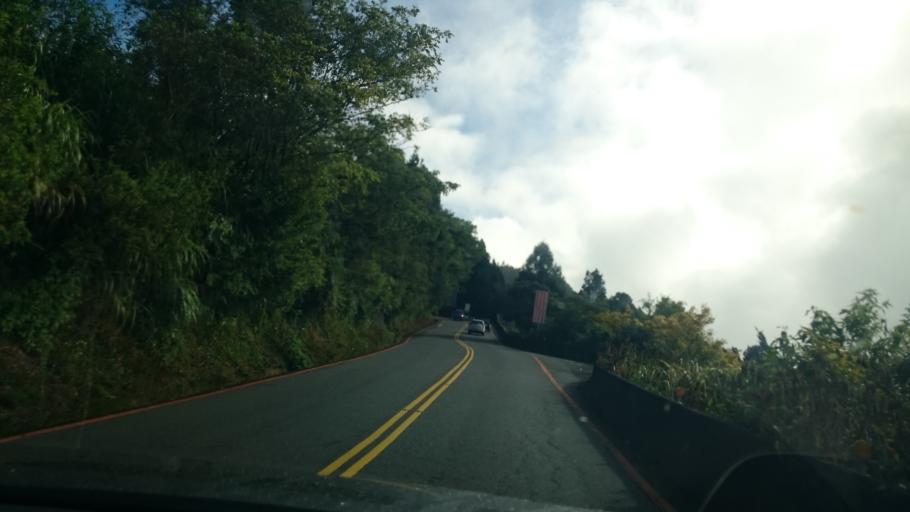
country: TW
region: Taiwan
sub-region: Nantou
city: Puli
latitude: 24.0583
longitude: 121.1644
